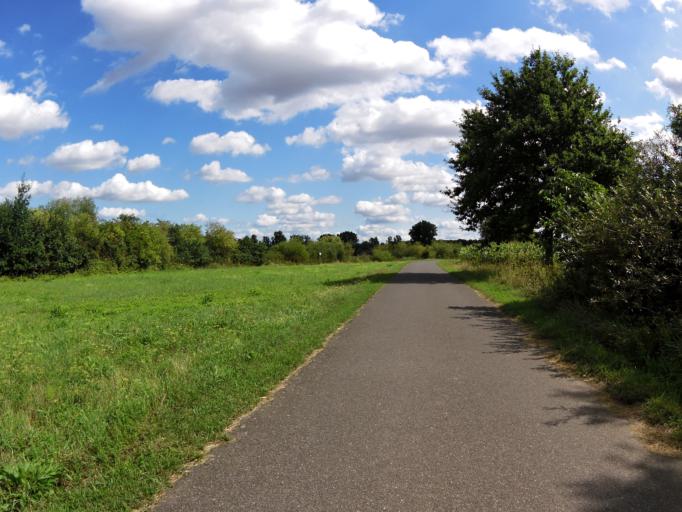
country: DE
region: Bavaria
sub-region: Regierungsbezirk Unterfranken
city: Volkach
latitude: 49.8540
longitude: 10.2152
